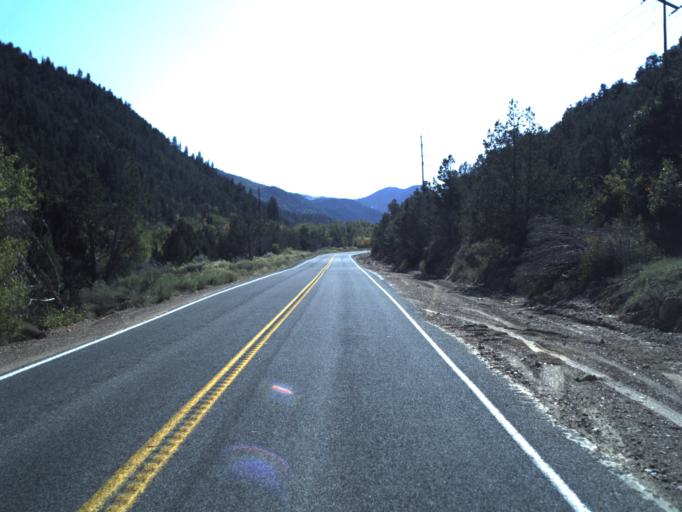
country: US
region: Utah
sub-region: Iron County
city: Parowan
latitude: 37.7938
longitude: -112.8187
